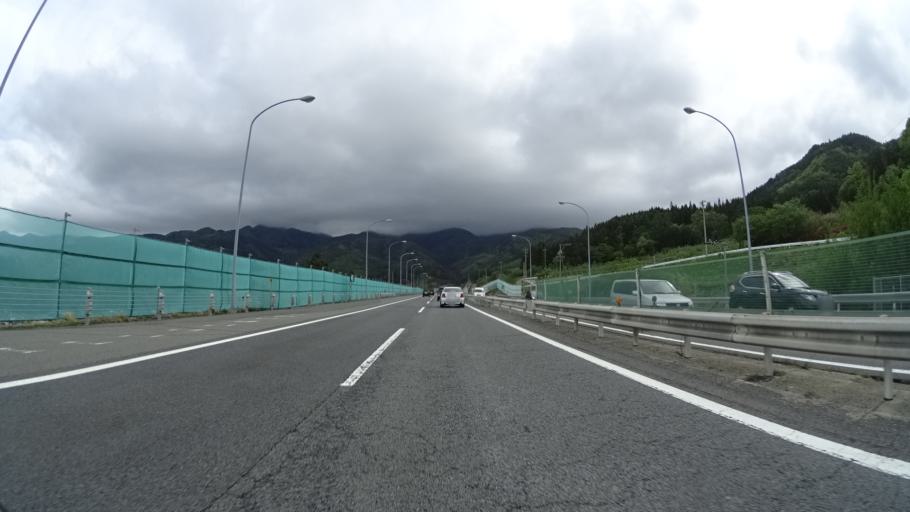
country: JP
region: Nagano
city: Nagano-shi
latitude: 36.5259
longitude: 138.0788
